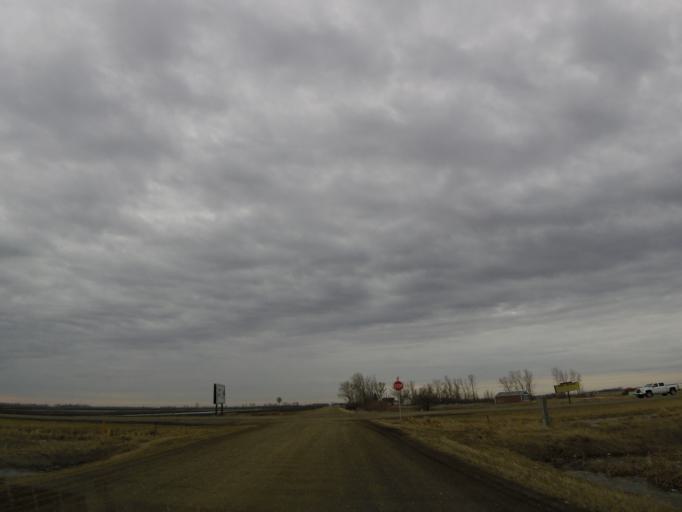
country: US
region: North Dakota
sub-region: Walsh County
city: Grafton
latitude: 48.4132
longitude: -97.4484
